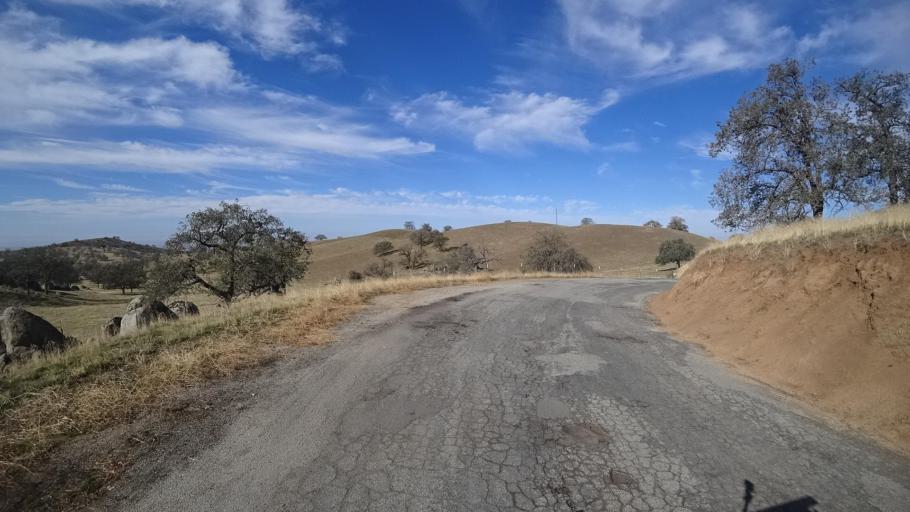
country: US
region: California
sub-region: Kern County
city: Oildale
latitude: 35.5912
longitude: -118.8252
